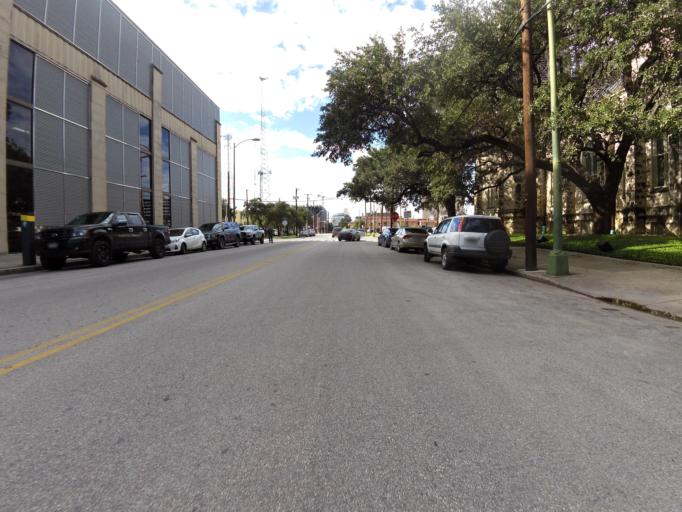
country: US
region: Texas
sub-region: Bexar County
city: San Antonio
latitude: 29.4286
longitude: -98.4848
